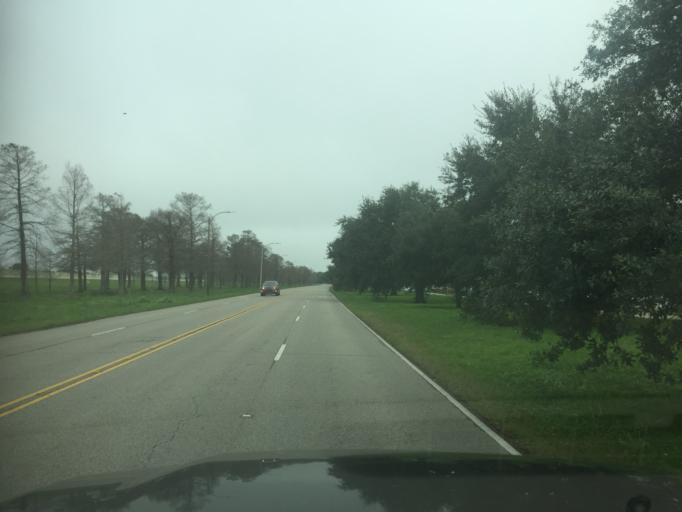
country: US
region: Louisiana
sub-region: Jefferson Parish
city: Metairie
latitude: 30.0124
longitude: -90.0981
